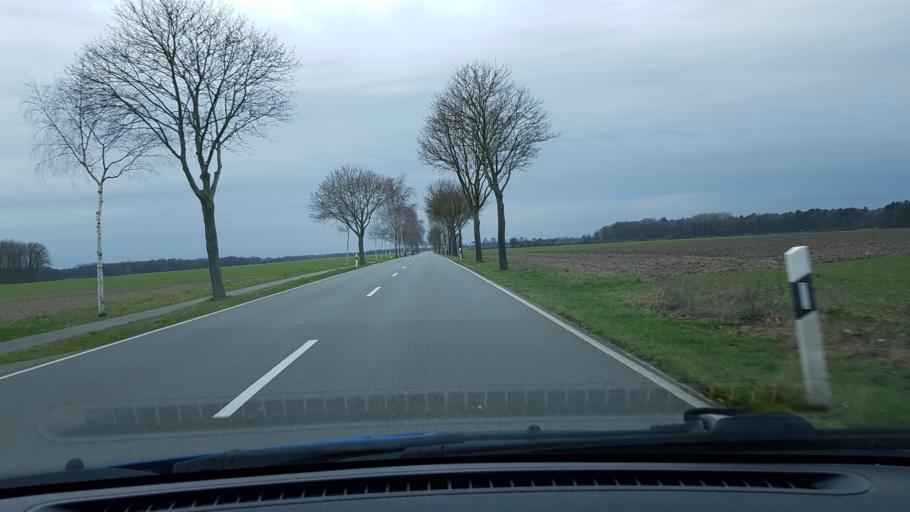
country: DE
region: Lower Saxony
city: Ratzlingen
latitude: 52.9748
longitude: 10.6533
